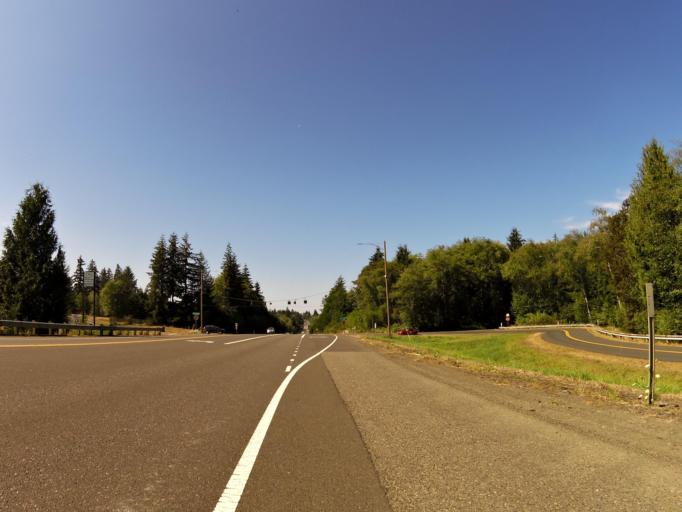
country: US
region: Oregon
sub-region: Clatsop County
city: Astoria
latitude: 46.1665
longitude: -123.6580
